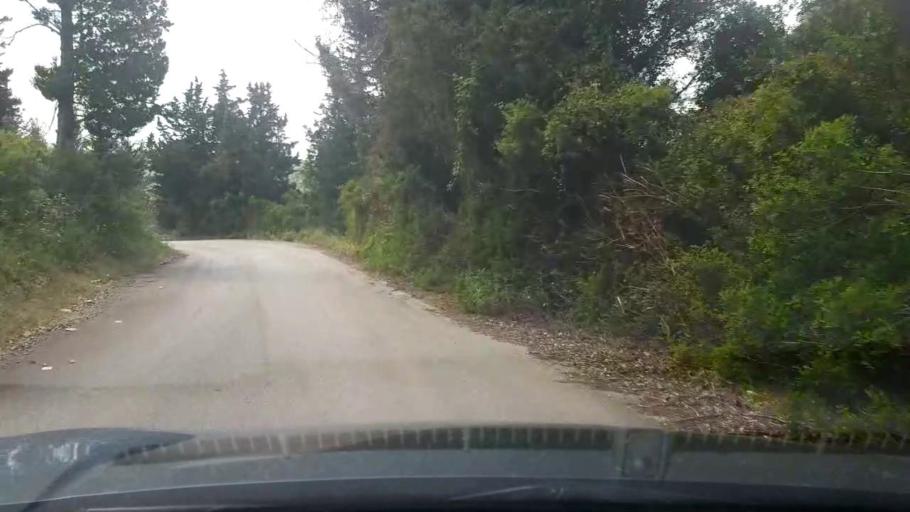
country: GR
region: Ionian Islands
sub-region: Lefkada
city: Nidri
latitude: 38.6452
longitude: 20.7014
